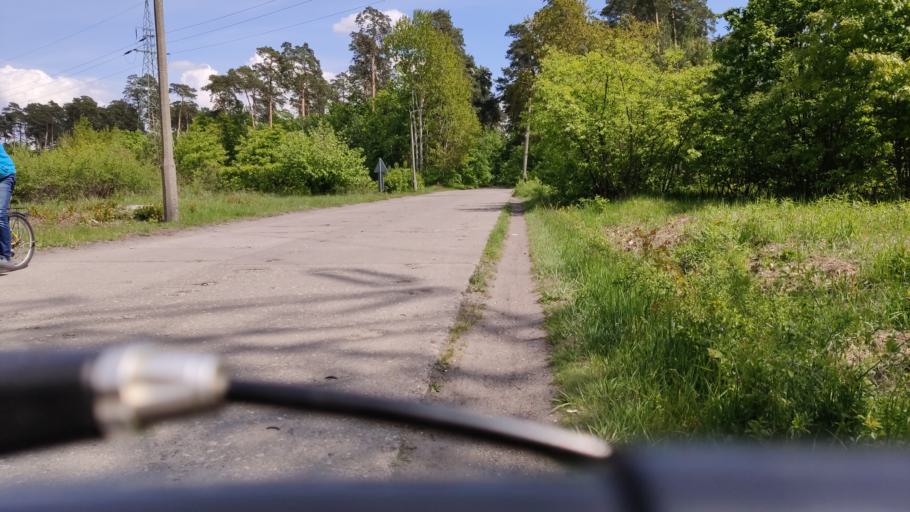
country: PL
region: Kujawsko-Pomorskie
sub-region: Wloclawek
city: Wloclawek
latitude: 52.6389
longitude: 19.0988
